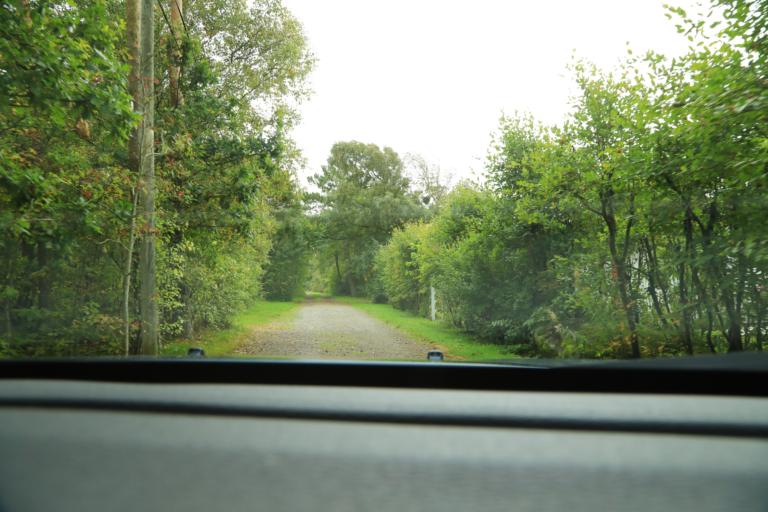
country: SE
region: Halland
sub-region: Varbergs Kommun
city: Tvaaker
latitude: 57.0204
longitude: 12.3389
